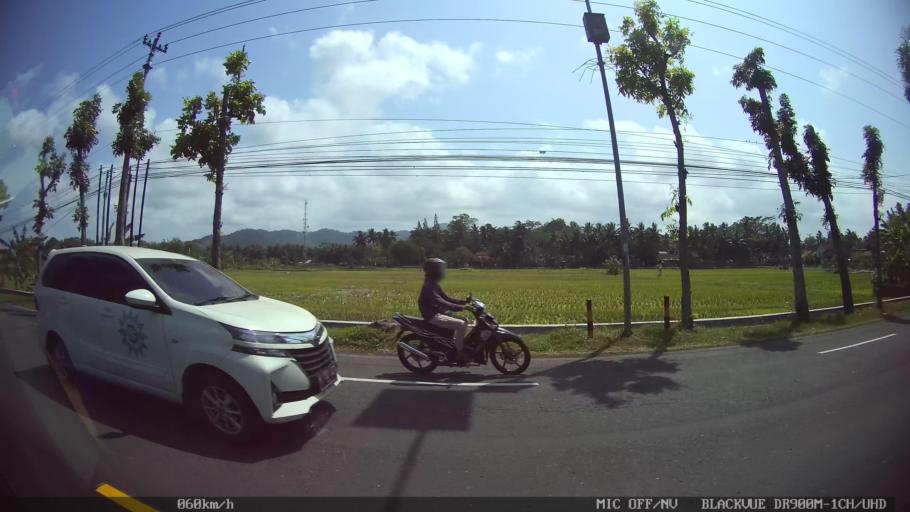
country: ID
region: Daerah Istimewa Yogyakarta
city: Srandakan
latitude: -7.8885
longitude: 110.0965
